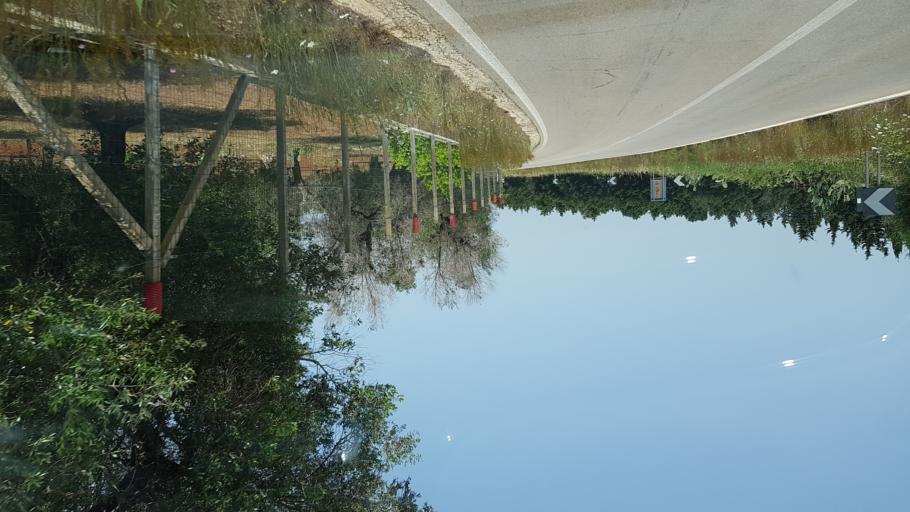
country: IT
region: Apulia
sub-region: Provincia di Lecce
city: Porto Cesareo
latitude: 40.3014
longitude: 17.9178
